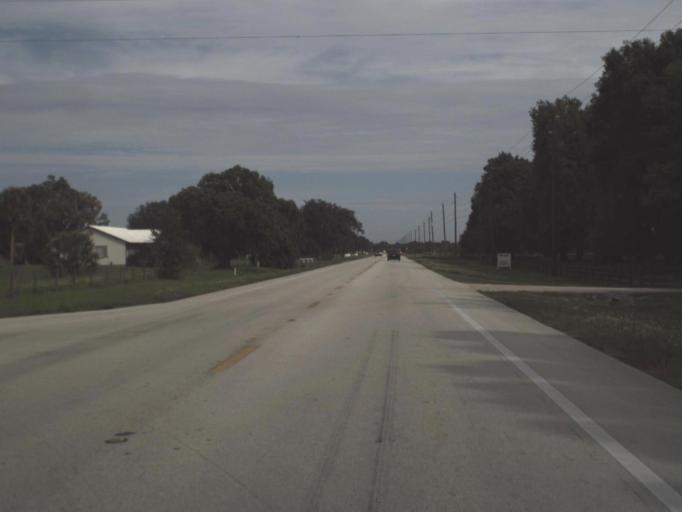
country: US
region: Florida
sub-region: DeSoto County
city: Southeast Arcadia
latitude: 27.1853
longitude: -81.8280
